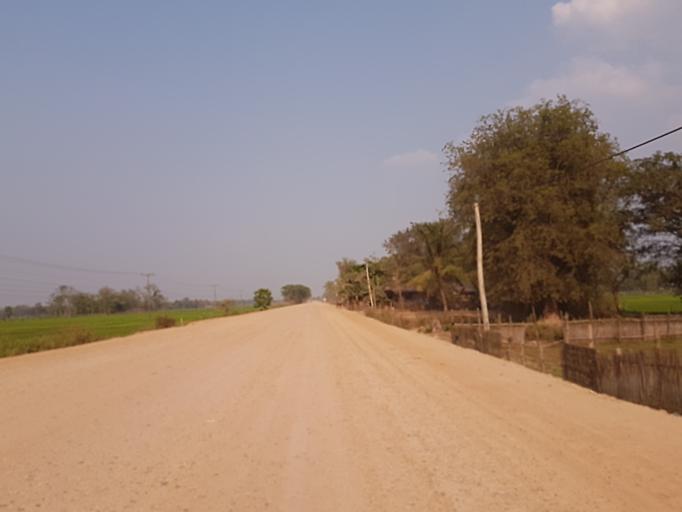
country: TH
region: Nong Khai
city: Phon Phisai
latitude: 17.9871
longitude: 102.8979
